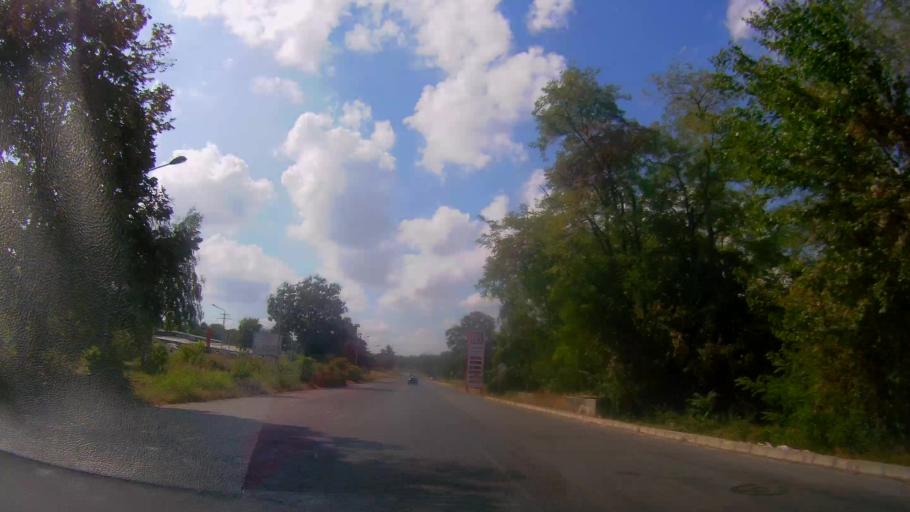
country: RO
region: Giurgiu
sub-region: Comuna Slobozia
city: Slobozia
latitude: 43.8164
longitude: 25.9294
